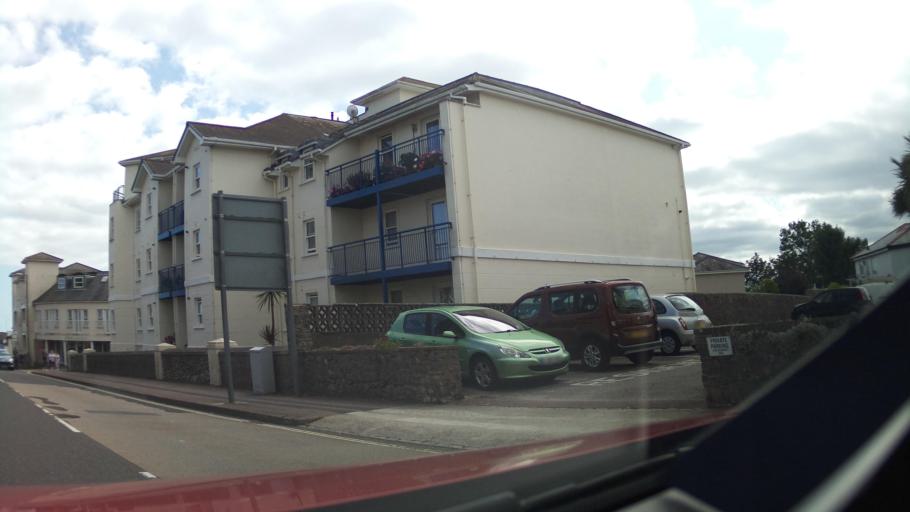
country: GB
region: England
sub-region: Borough of Torbay
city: Torquay
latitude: 50.4802
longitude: -3.5184
